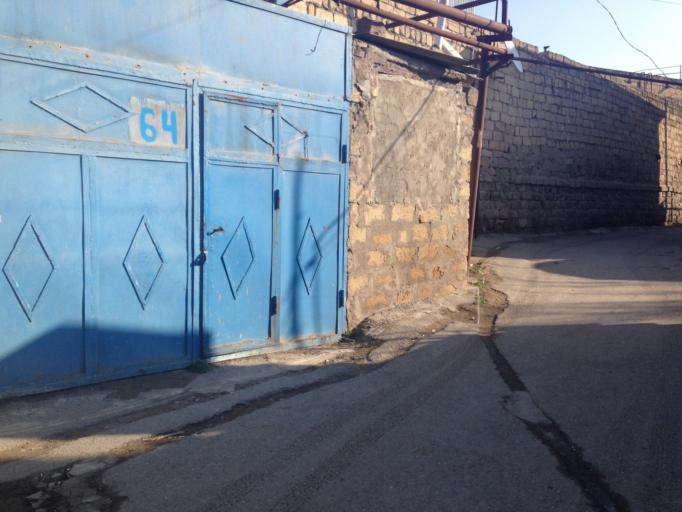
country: AZ
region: Baki
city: Baku
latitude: 40.3954
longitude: 49.8820
